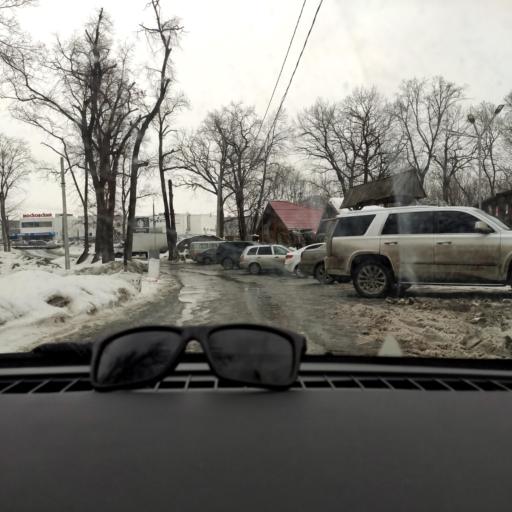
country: RU
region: Samara
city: Petra-Dubrava
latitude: 53.2726
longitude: 50.2676
